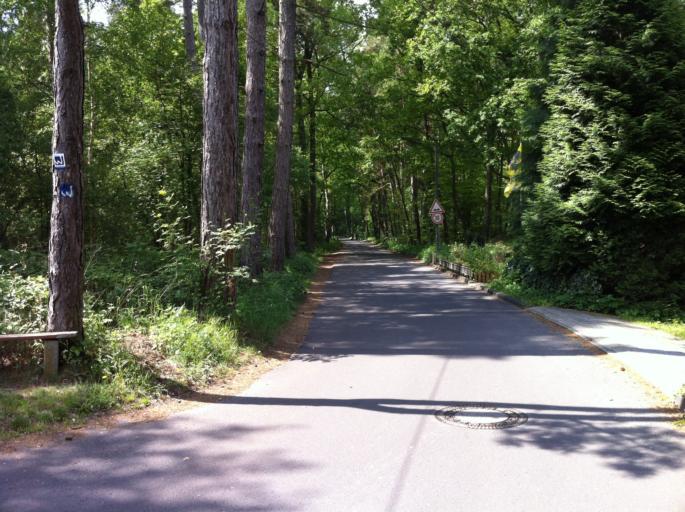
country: DE
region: North Rhine-Westphalia
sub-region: Regierungsbezirk Koln
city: Wassenberg
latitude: 51.1160
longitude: 6.1670
